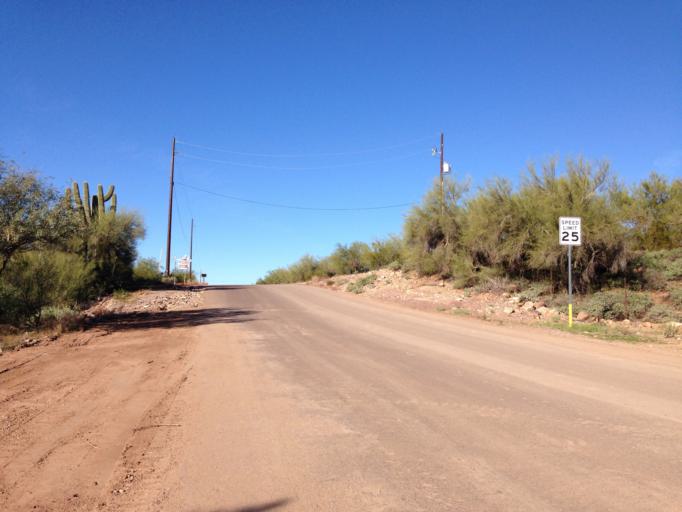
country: US
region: Arizona
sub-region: Maricopa County
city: New River
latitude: 33.8952
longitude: -112.0684
